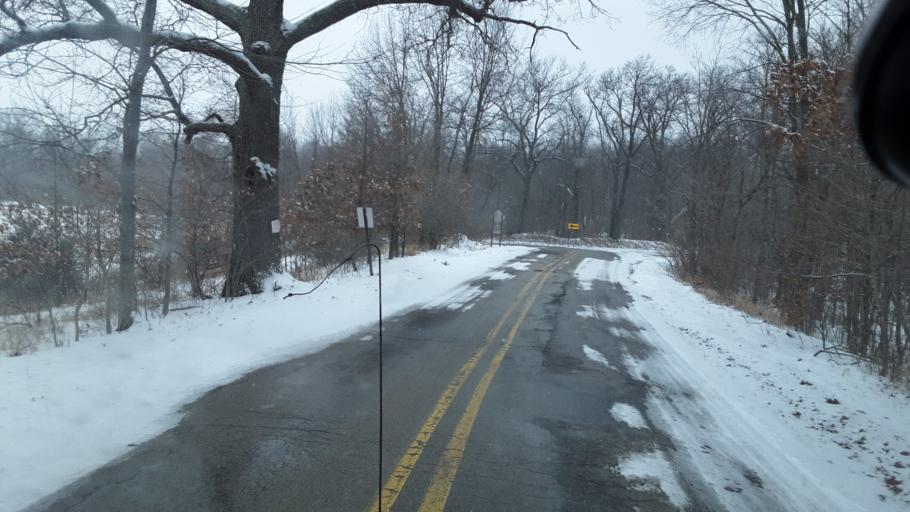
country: US
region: Michigan
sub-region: Ingham County
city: Leslie
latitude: 42.4904
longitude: -84.3666
